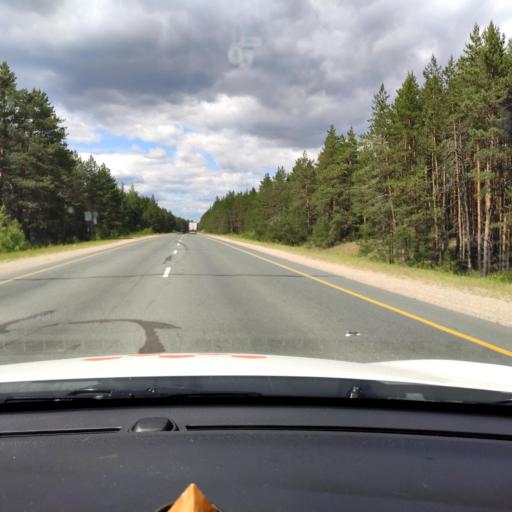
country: RU
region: Mariy-El
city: Krasnogorskiy
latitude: 56.0905
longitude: 48.3493
